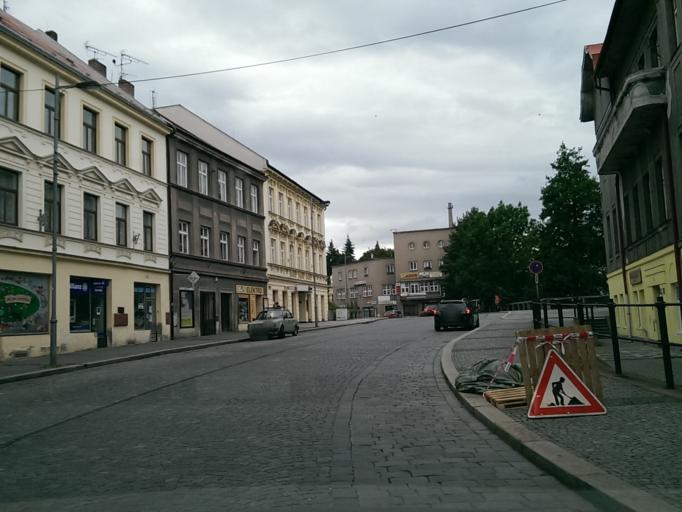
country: CZ
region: Liberecky
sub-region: Okres Semily
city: Turnov
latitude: 50.5870
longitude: 15.1530
